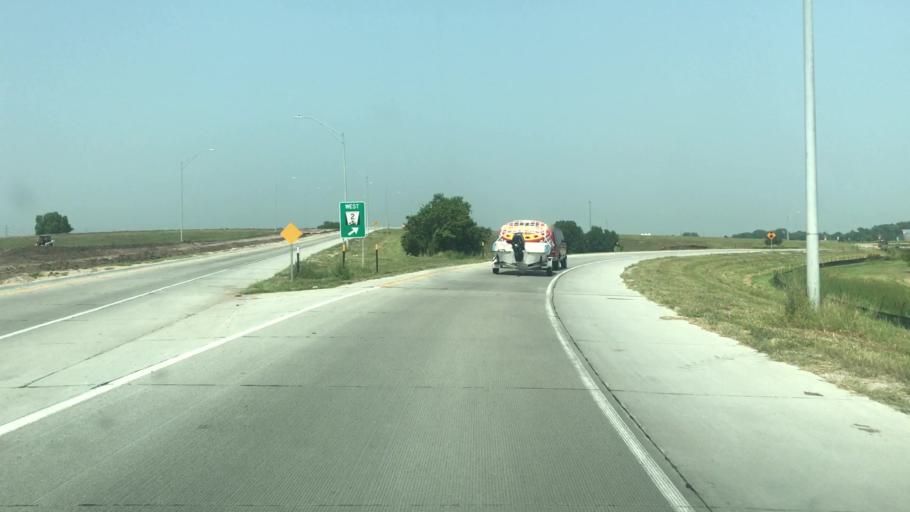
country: US
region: Nebraska
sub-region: Hall County
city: Grand Island
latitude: 40.9500
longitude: -98.3840
